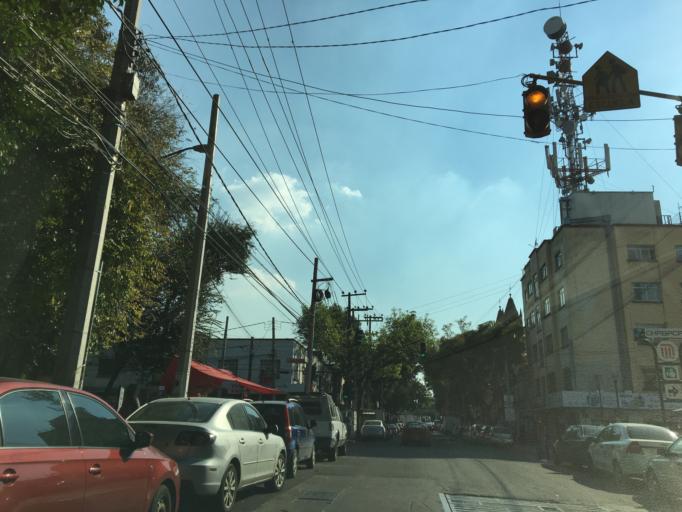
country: MX
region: Mexico City
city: Mexico City
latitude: 19.4105
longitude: -99.1332
